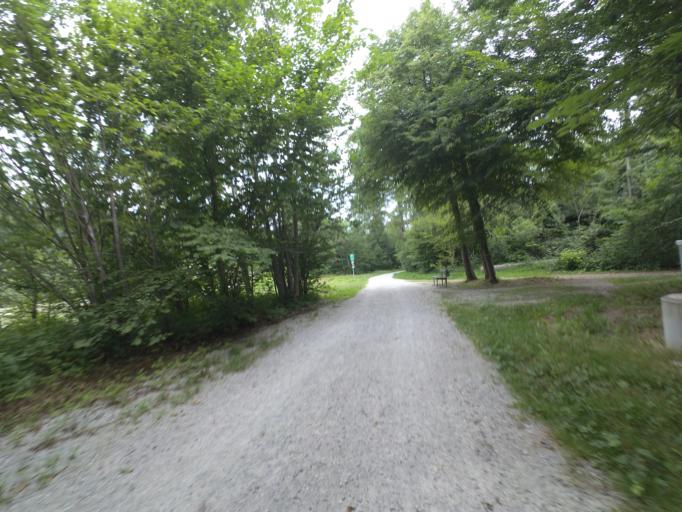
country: DE
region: Bavaria
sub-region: Upper Bavaria
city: Piding
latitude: 47.7829
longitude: 12.9395
